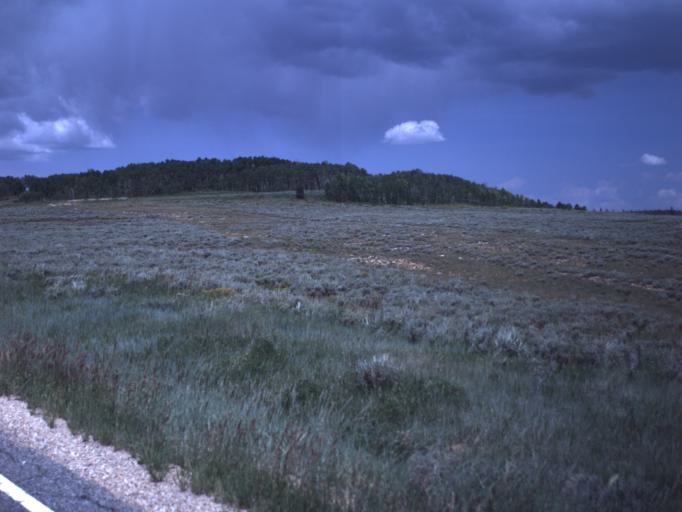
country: US
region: Utah
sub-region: Sanpete County
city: Fairview
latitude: 39.6713
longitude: -111.3090
